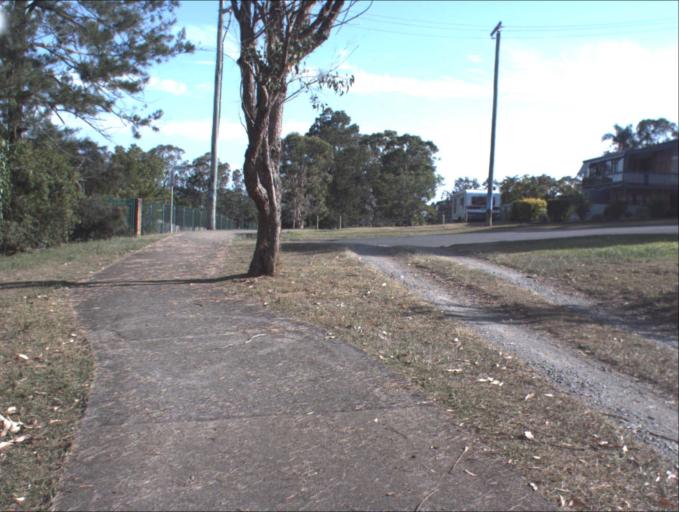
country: AU
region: Queensland
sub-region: Logan
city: Beenleigh
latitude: -27.6778
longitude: 153.2056
